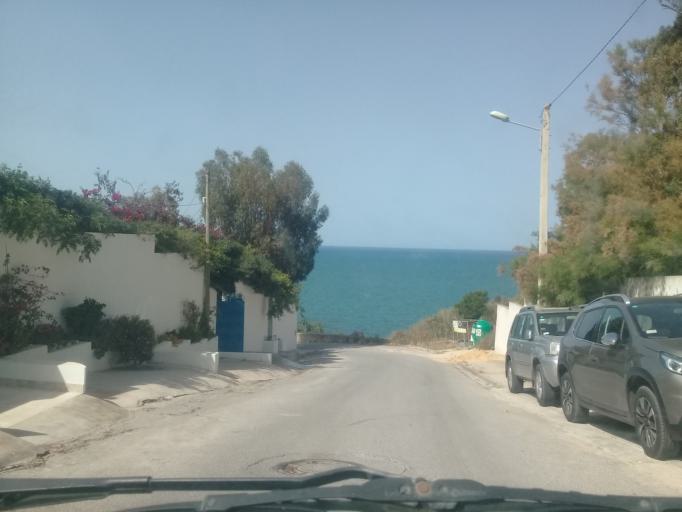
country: TN
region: Tunis
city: Sidi Bou Said
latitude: 36.8799
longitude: 10.3409
